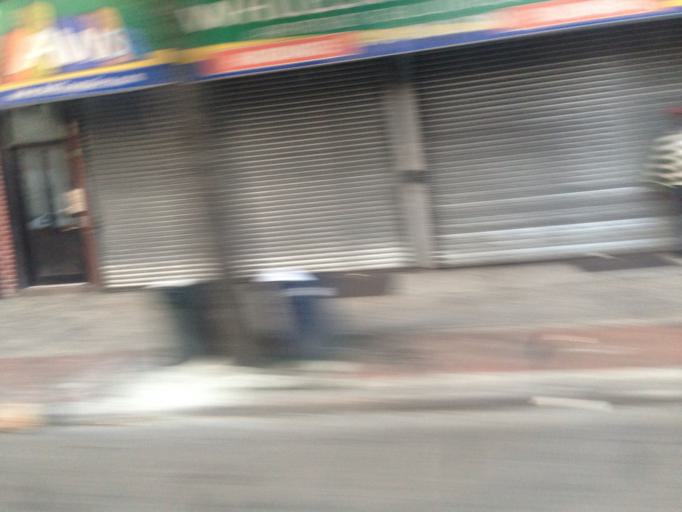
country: US
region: New York
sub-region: Kings County
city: Brooklyn
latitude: 40.6386
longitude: -73.9536
